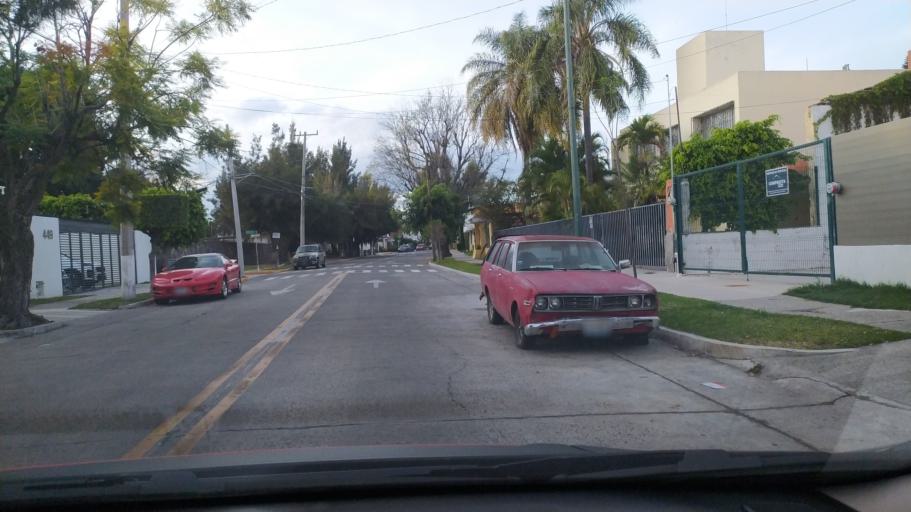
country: MX
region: Jalisco
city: Guadalajara
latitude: 20.6598
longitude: -103.4029
